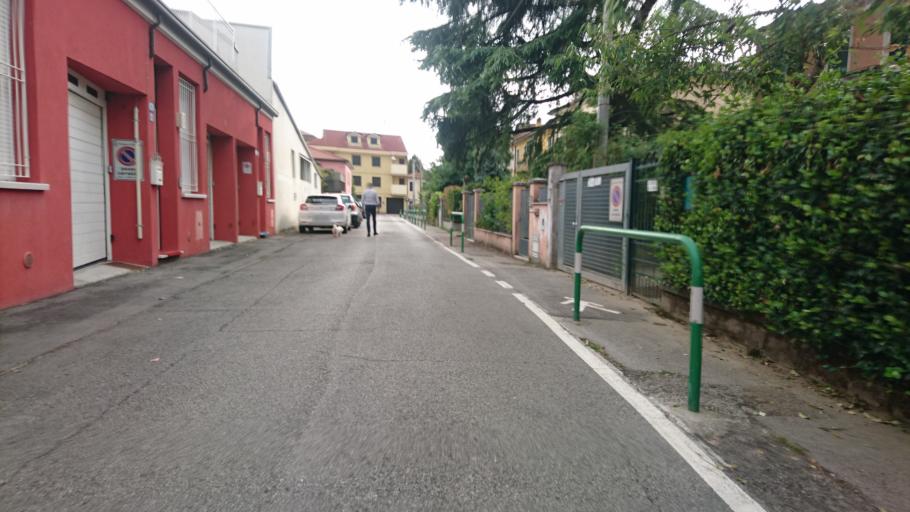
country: IT
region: Veneto
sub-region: Provincia di Padova
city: Padova
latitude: 45.4080
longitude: 11.8550
